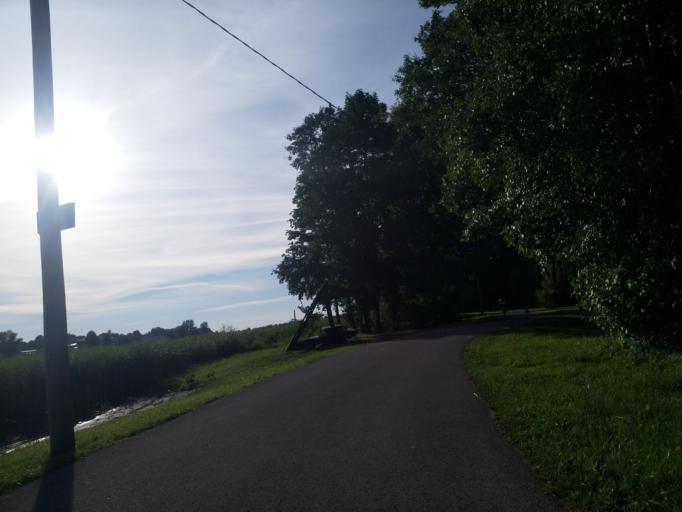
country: EE
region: Paernumaa
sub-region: Paernu linn
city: Parnu
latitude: 58.3837
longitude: 24.5363
